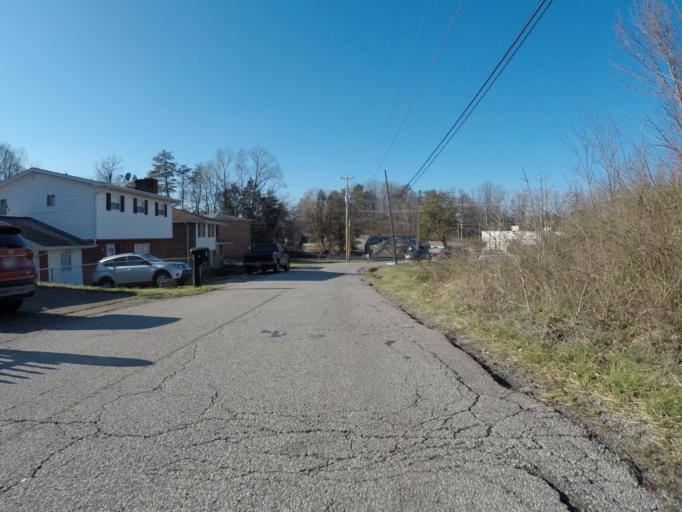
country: US
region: West Virginia
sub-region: Cabell County
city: Pea Ridge
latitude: 38.4097
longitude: -82.3263
